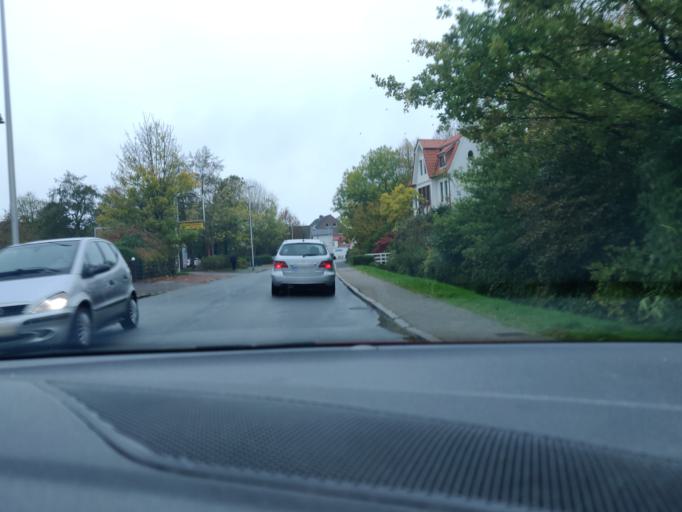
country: DE
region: Lower Saxony
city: Cuxhaven
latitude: 53.8805
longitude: 8.6794
